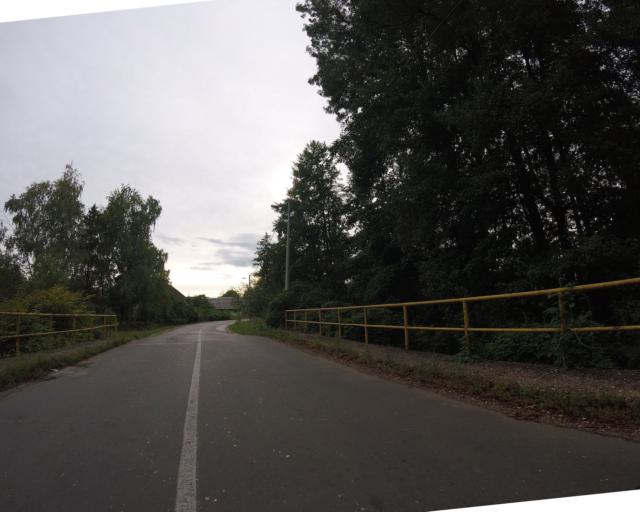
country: HR
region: Zagrebacka
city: Kuce
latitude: 45.7060
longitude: 16.1443
